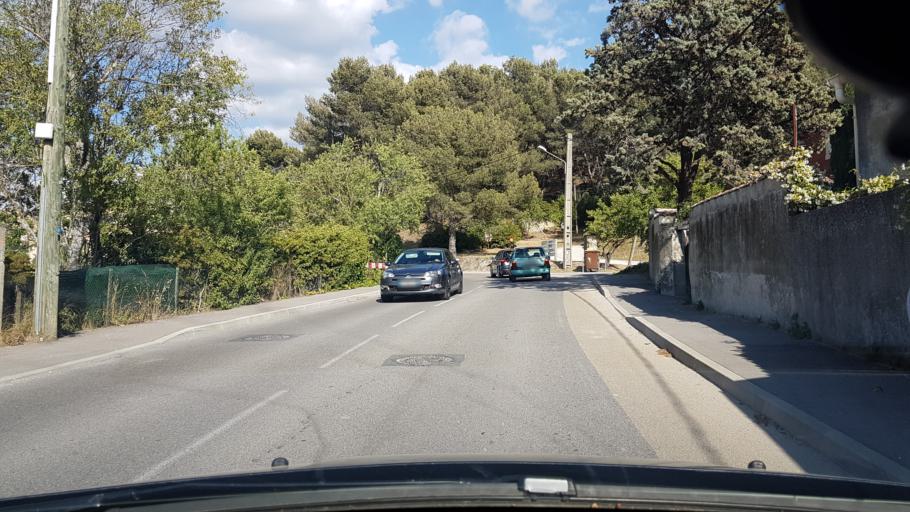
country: FR
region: Provence-Alpes-Cote d'Azur
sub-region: Departement des Bouches-du-Rhone
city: Carnoux-en-Provence
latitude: 43.2475
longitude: 5.5732
